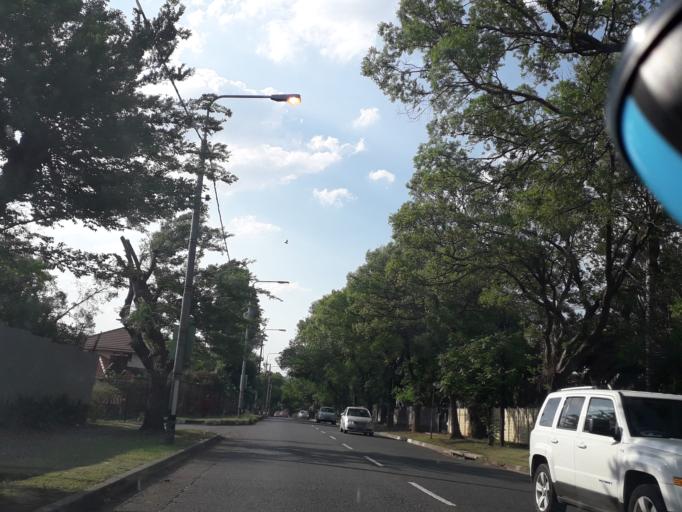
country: ZA
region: Gauteng
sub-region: City of Johannesburg Metropolitan Municipality
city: Johannesburg
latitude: -26.1397
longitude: 28.0746
